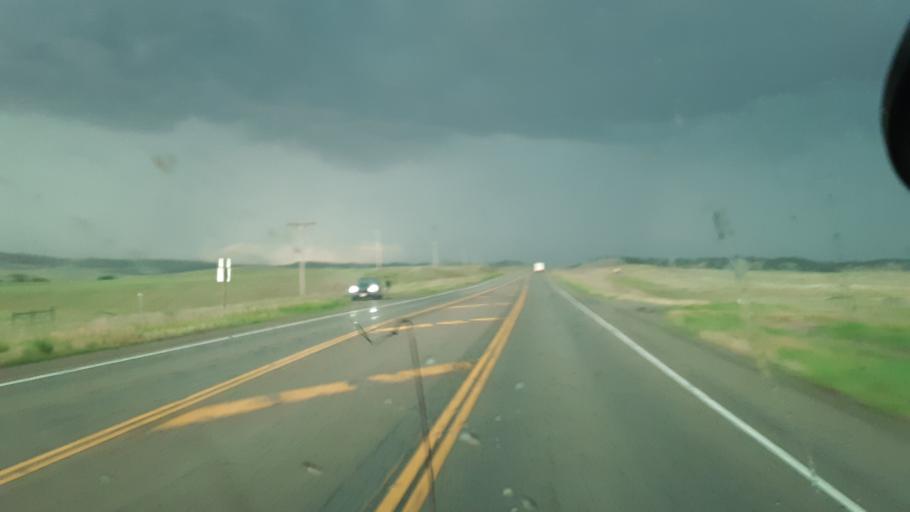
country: US
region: Montana
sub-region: Powder River County
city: Broadus
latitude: 45.4667
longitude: -105.4646
